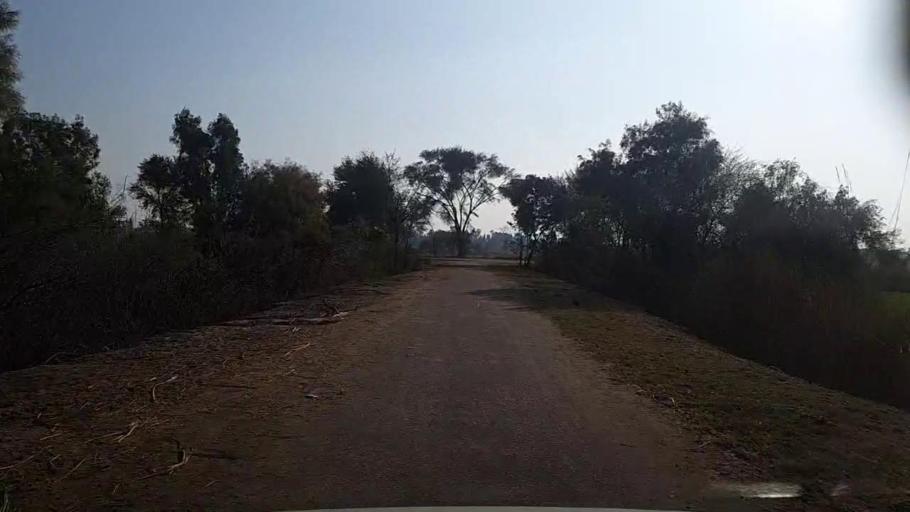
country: PK
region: Sindh
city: Mirpur Mathelo
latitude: 27.8758
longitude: 69.6257
